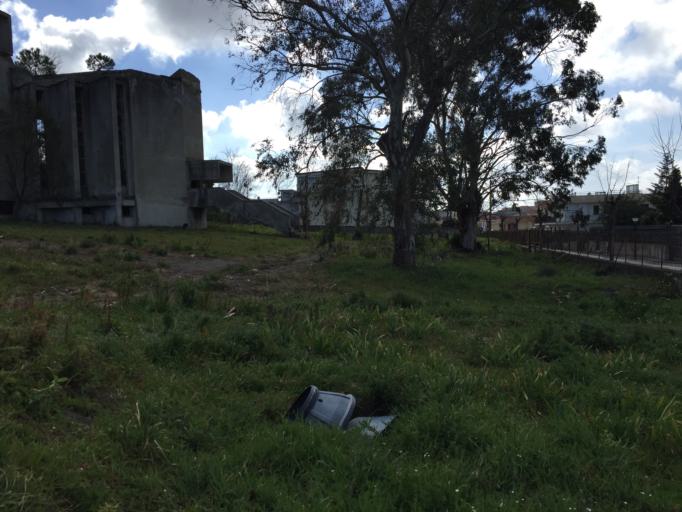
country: IT
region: Campania
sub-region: Provincia di Napoli
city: Pollena Trocchia
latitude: 40.8510
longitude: 14.3787
